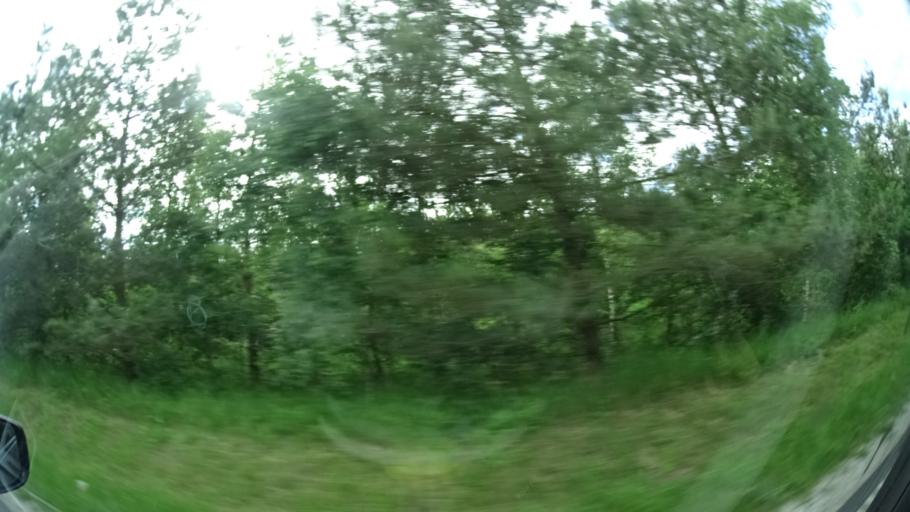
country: DK
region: Central Jutland
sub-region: Syddjurs Kommune
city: Ryomgard
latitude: 56.3566
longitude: 10.4921
